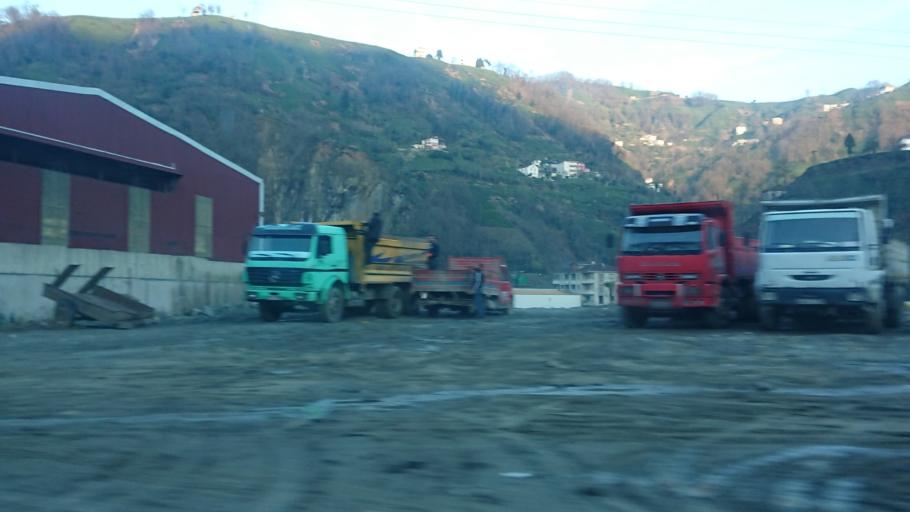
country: TR
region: Rize
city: Gundogdu
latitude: 41.0270
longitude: 40.5806
